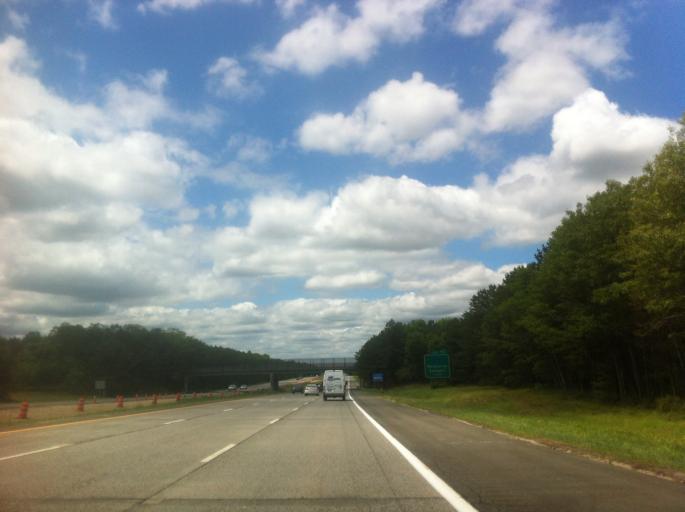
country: US
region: New York
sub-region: Suffolk County
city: Manorville
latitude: 40.8783
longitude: -72.7791
